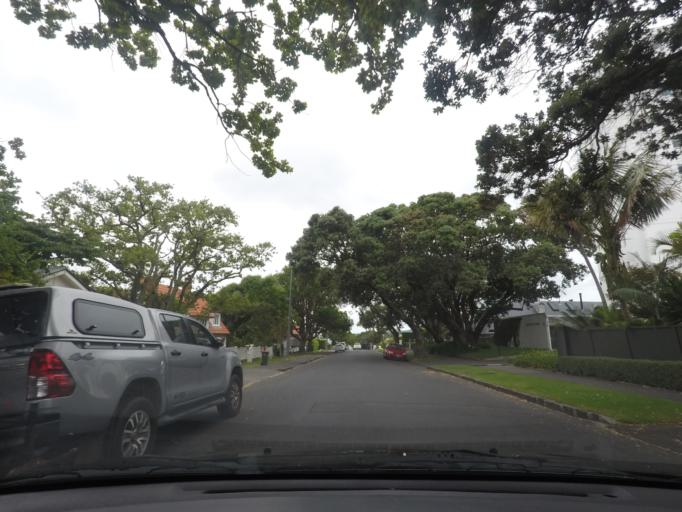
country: NZ
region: Auckland
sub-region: Auckland
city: Auckland
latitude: -36.8520
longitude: 174.7904
